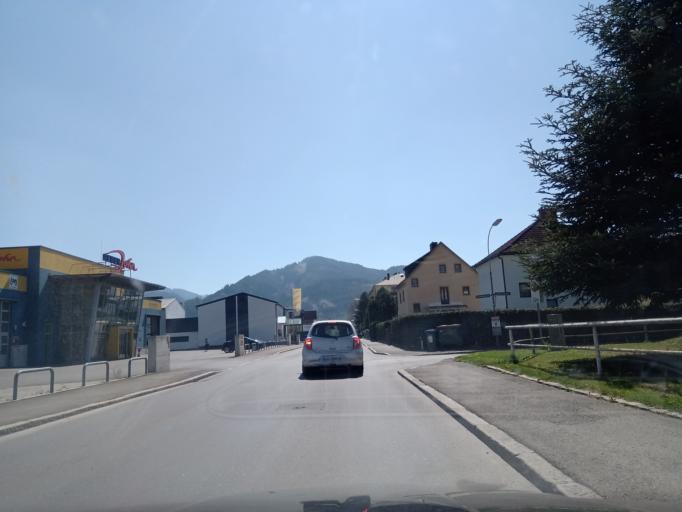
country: AT
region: Styria
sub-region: Politischer Bezirk Leoben
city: Leoben
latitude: 47.3719
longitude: 15.0850
